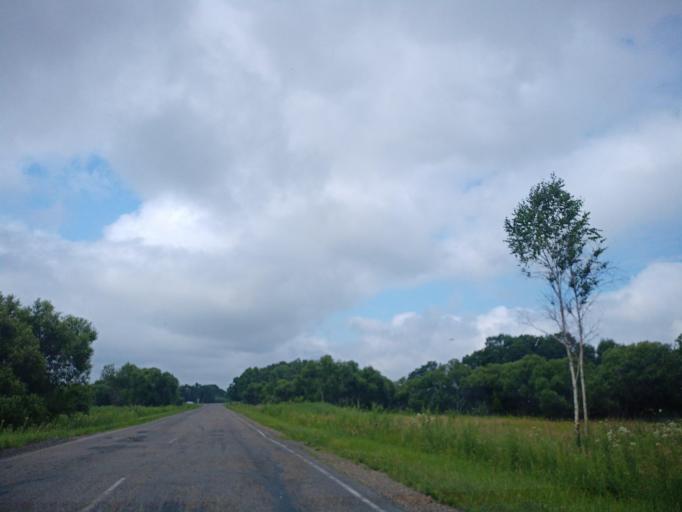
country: RU
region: Primorskiy
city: Dal'nerechensk
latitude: 45.9391
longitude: 133.8718
